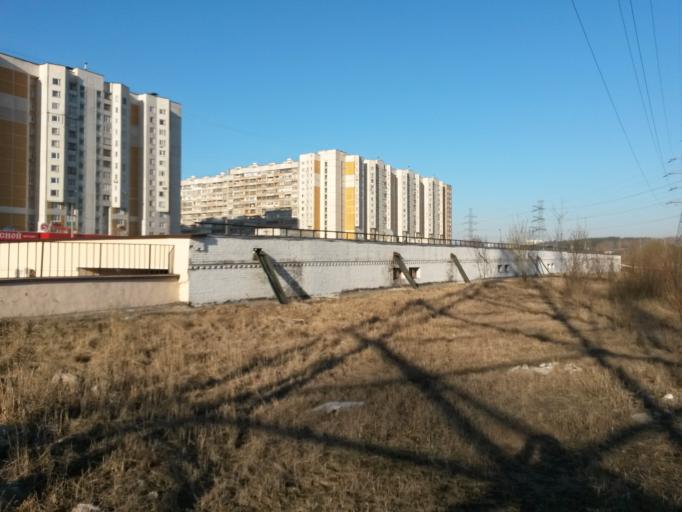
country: RU
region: Moscow
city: Chertanovo Yuzhnoye
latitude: 55.5787
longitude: 37.5783
